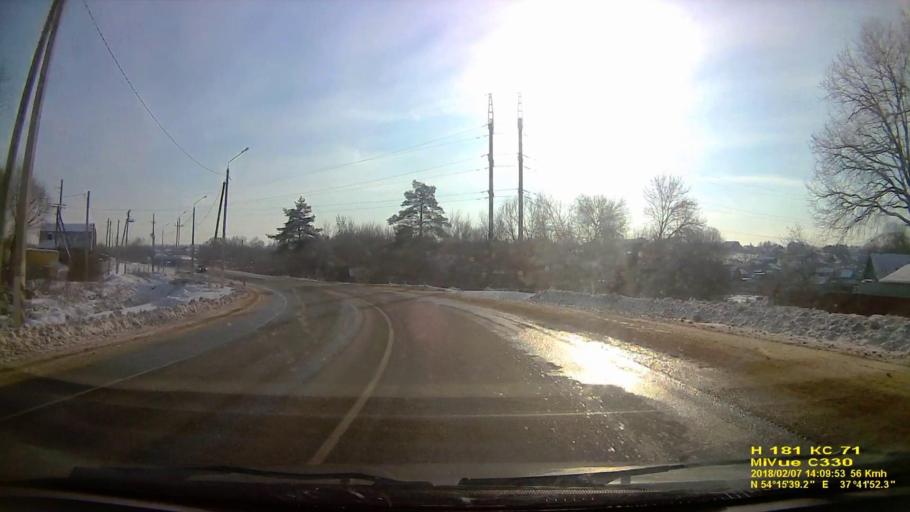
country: RU
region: Tula
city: Gorelki
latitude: 54.2607
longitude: 37.6977
